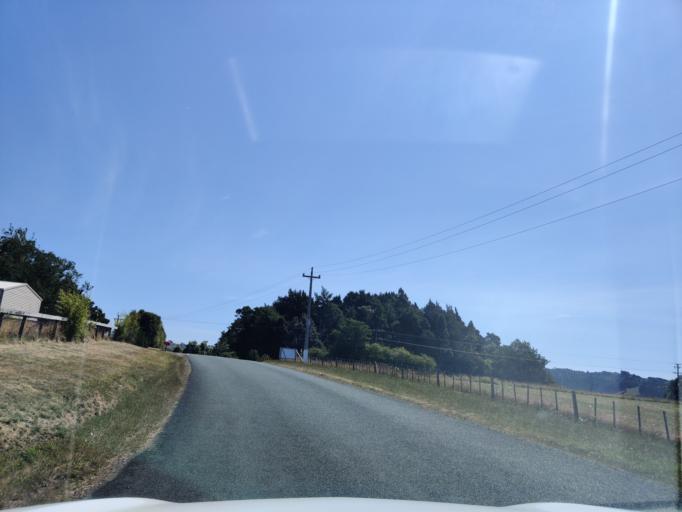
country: NZ
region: Auckland
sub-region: Auckland
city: Red Hill
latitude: -37.0688
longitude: 175.0716
